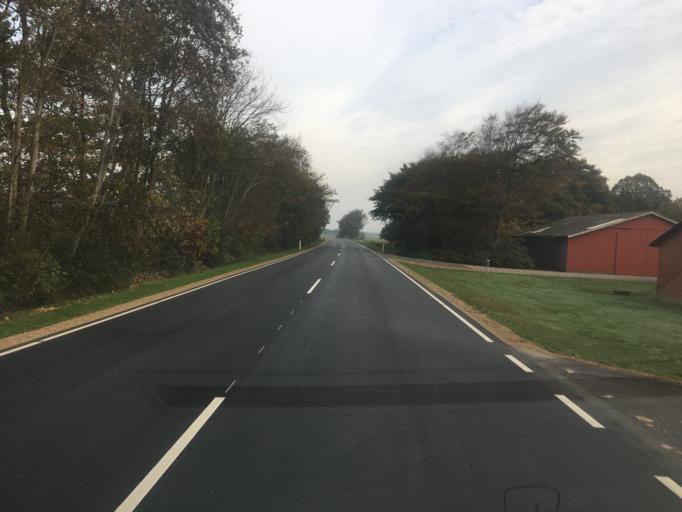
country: DK
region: South Denmark
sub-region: Tonder Kommune
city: Logumkloster
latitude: 55.0956
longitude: 9.0227
